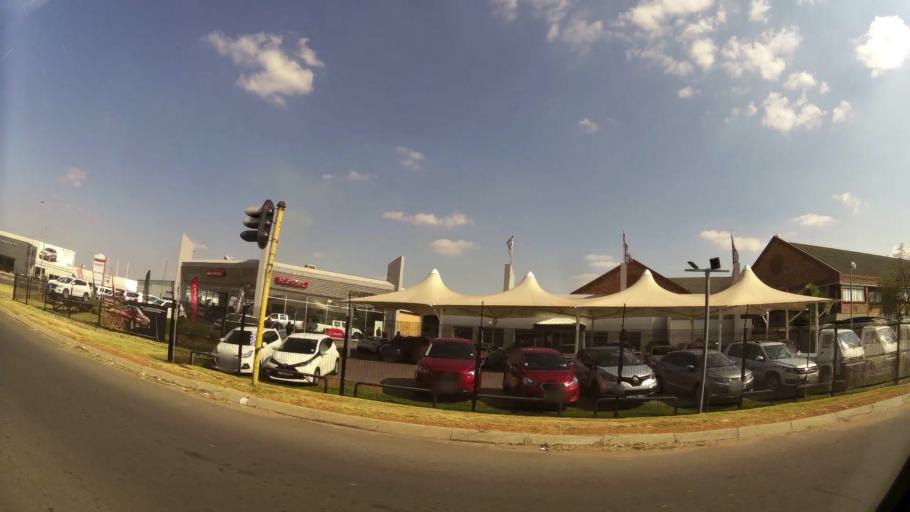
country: ZA
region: Gauteng
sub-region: Ekurhuleni Metropolitan Municipality
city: Boksburg
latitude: -26.1808
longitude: 28.2442
